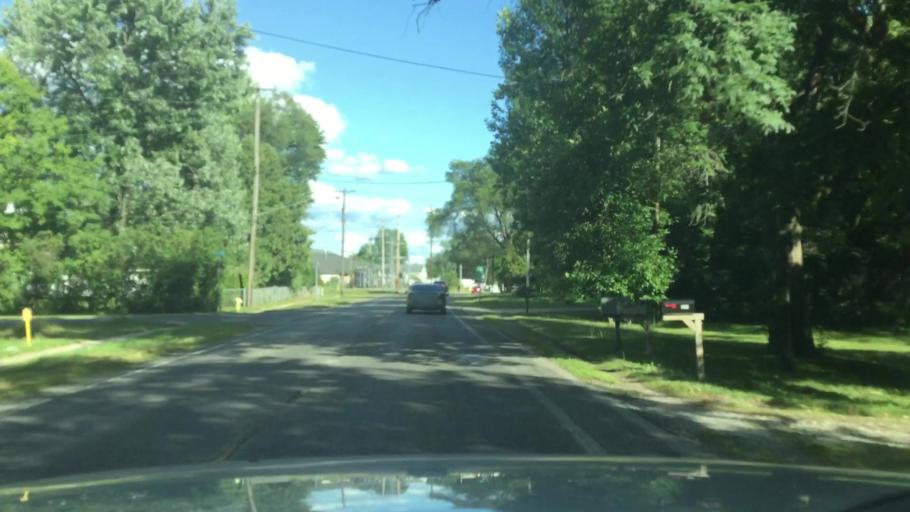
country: US
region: Michigan
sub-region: Saginaw County
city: Bridgeport
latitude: 43.3610
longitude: -83.8860
